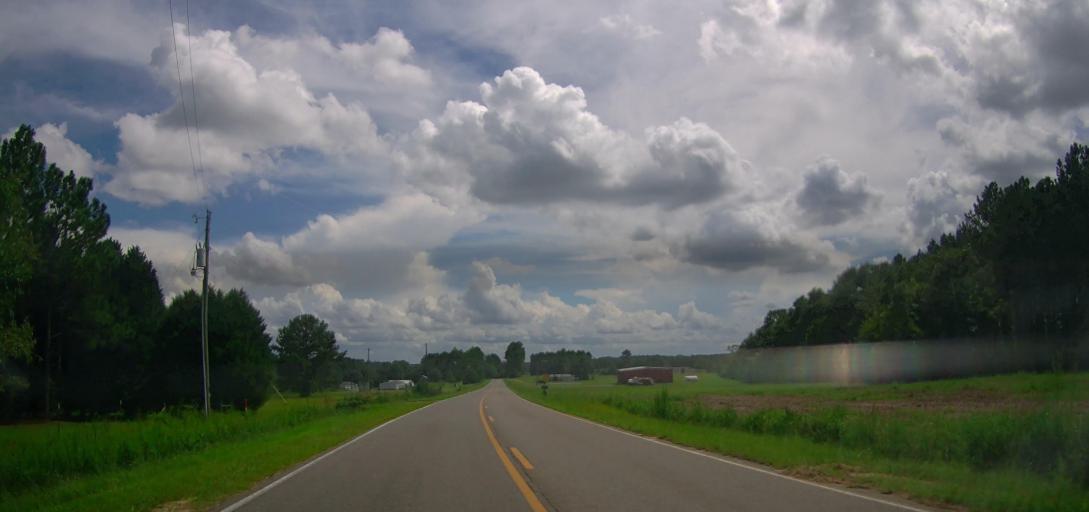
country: US
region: Georgia
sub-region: Taylor County
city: Butler
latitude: 32.4694
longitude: -84.2006
